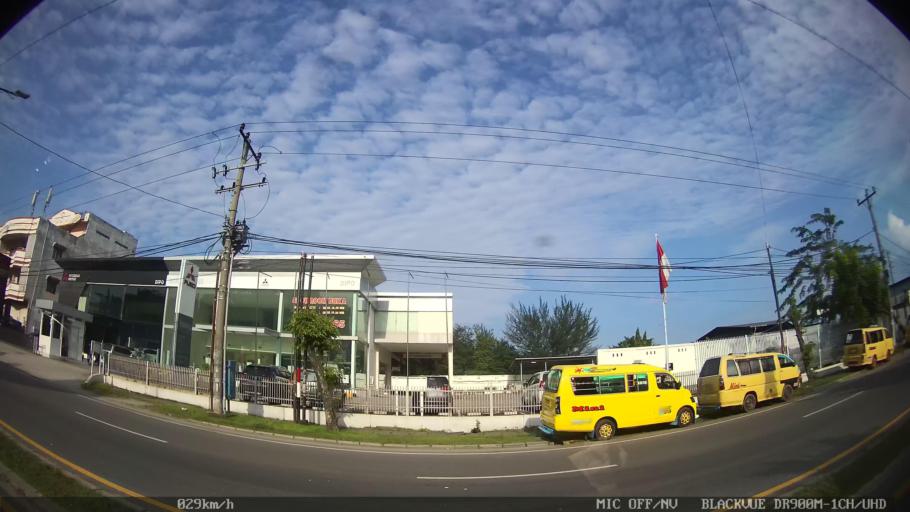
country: ID
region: North Sumatra
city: Medan
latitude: 3.6412
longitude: 98.6818
